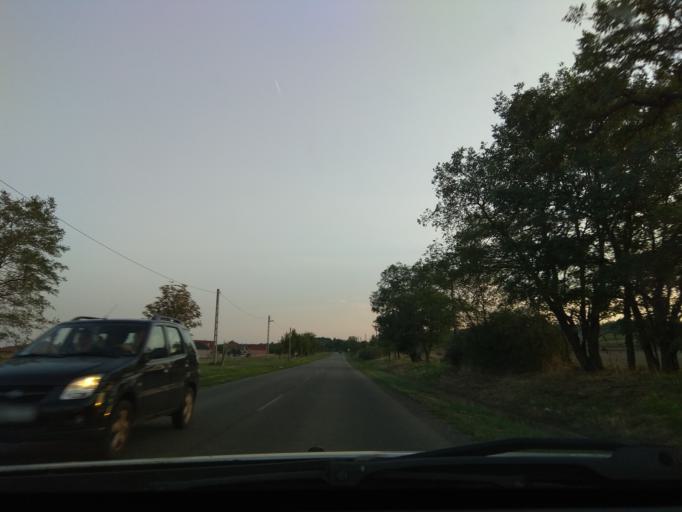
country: HU
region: Borsod-Abauj-Zemplen
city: Szerencs
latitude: 48.1788
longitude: 21.2047
